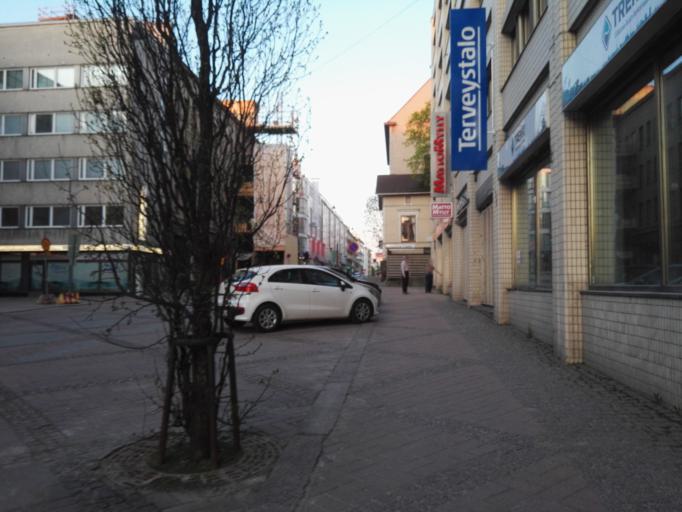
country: FI
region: Paijanne Tavastia
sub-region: Lahti
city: Lahti
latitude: 60.9819
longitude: 25.6567
